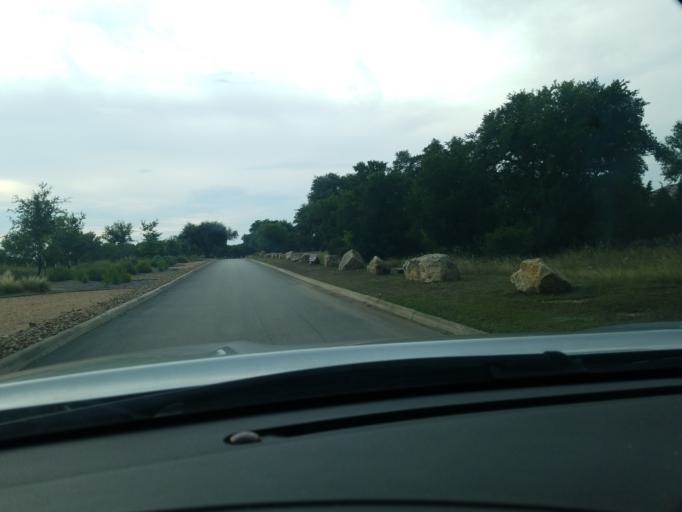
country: US
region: Texas
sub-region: Comal County
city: Bulverde
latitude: 29.8476
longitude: -98.4030
